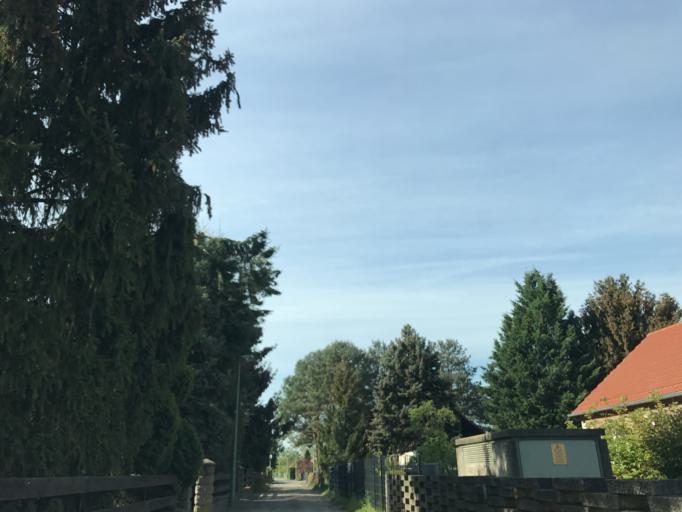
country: DE
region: Berlin
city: Staaken
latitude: 52.5434
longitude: 13.1400
